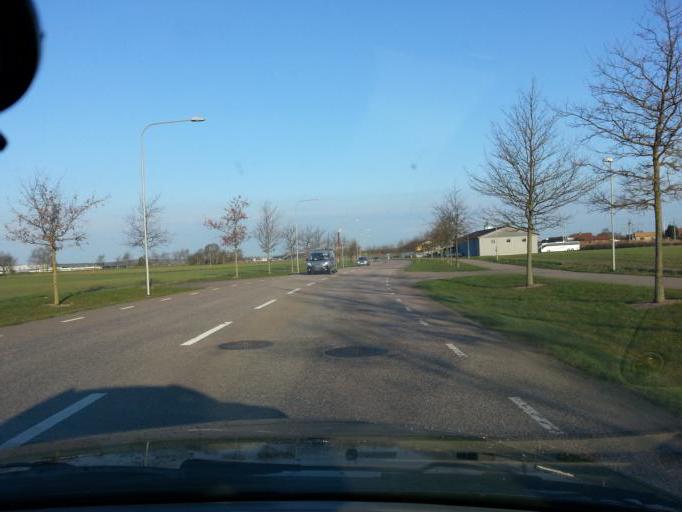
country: SE
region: Skane
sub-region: Klippans Kommun
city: Klippan
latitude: 56.1286
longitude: 13.1470
